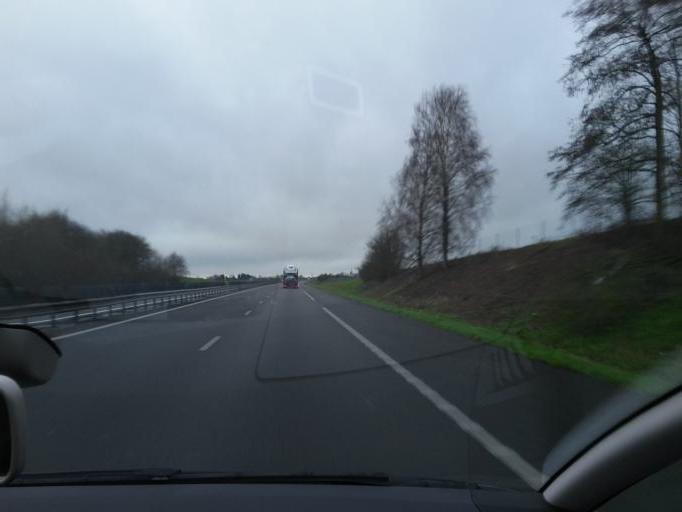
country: FR
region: Nord-Pas-de-Calais
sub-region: Departement du Pas-de-Calais
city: Hermies
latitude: 50.0844
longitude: 3.0355
